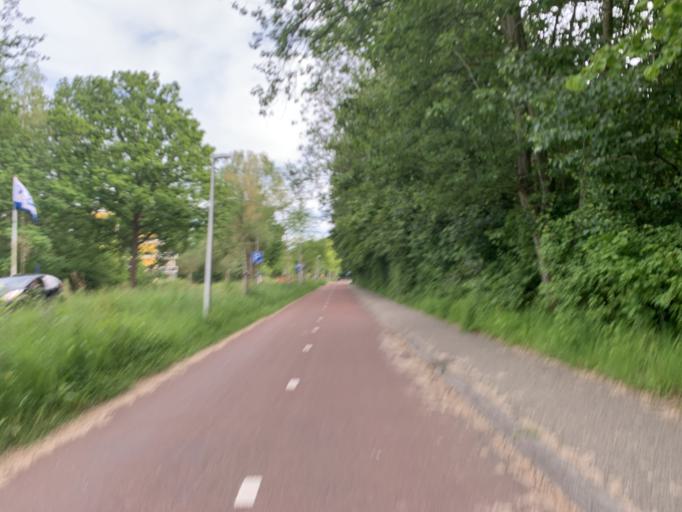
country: NL
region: Groningen
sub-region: Gemeente Haren
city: Haren
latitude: 53.1795
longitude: 6.6042
